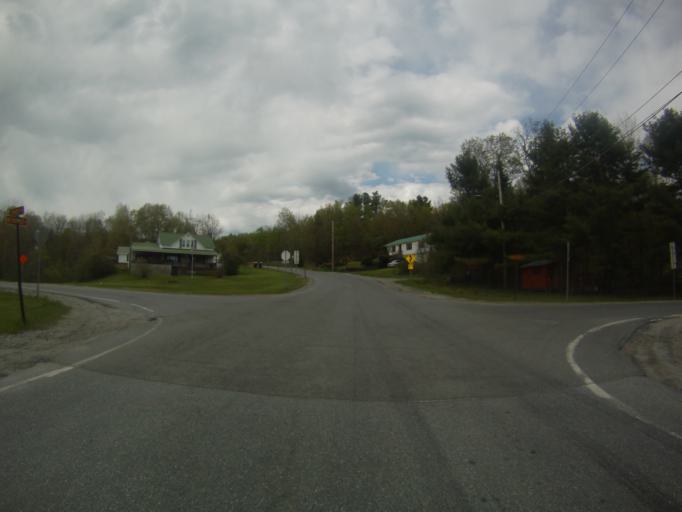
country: US
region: New York
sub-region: Essex County
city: Mineville
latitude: 44.0898
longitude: -73.5372
